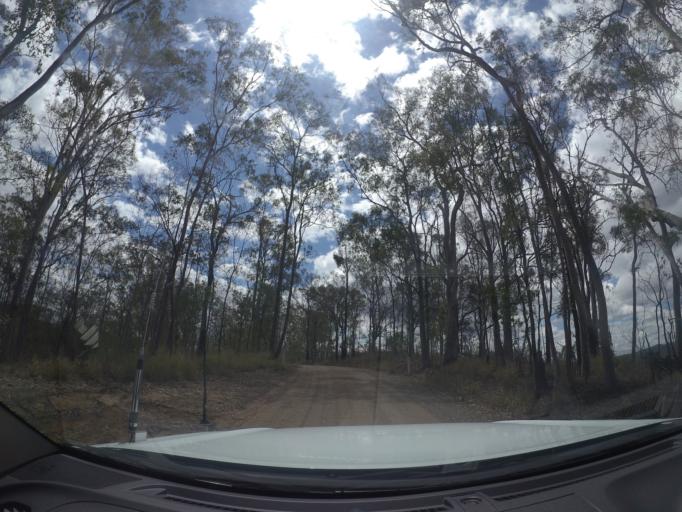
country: AU
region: Queensland
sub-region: Logan
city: Cedar Vale
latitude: -27.8926
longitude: 153.0455
